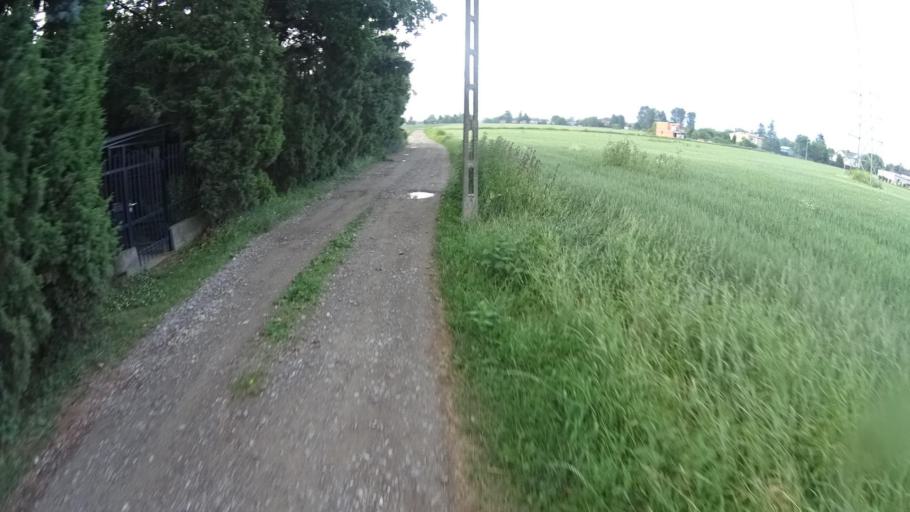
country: PL
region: Masovian Voivodeship
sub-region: Powiat warszawski zachodni
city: Babice
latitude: 52.2204
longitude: 20.8549
